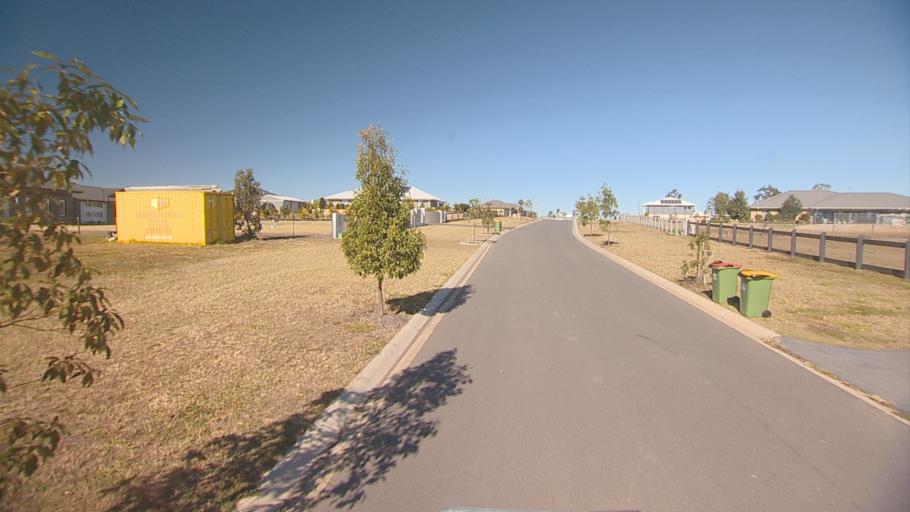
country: AU
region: Queensland
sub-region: Logan
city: North Maclean
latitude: -27.7484
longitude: 152.9471
